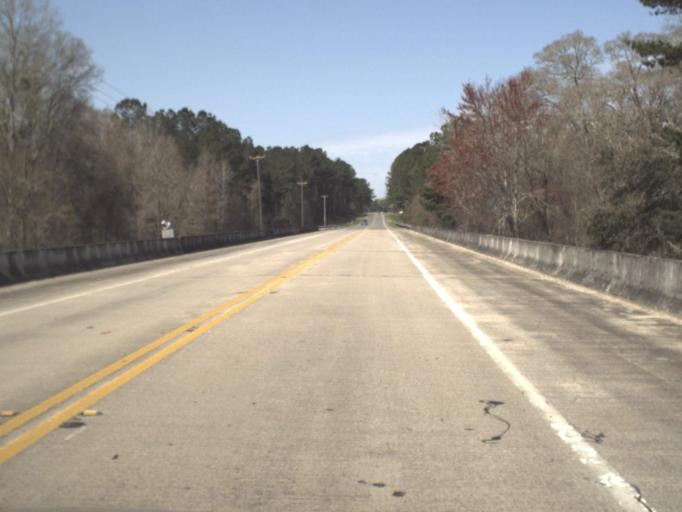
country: US
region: Florida
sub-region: Gadsden County
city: Quincy
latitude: 30.5872
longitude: -84.4959
